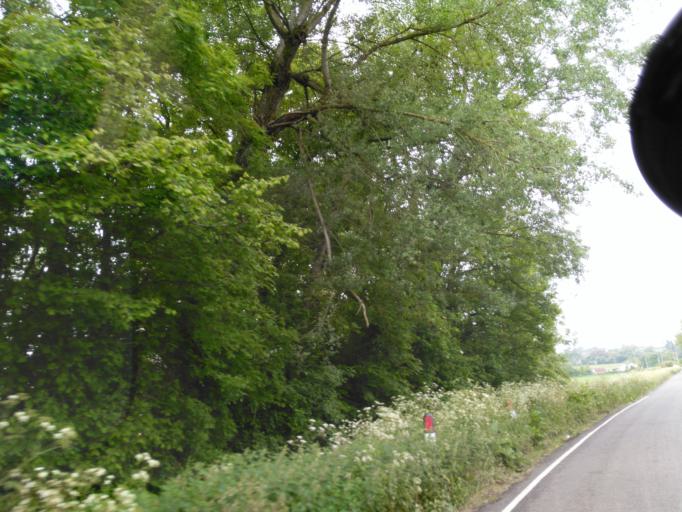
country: GB
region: England
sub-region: Somerset
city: Langport
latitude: 51.1181
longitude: -2.8253
